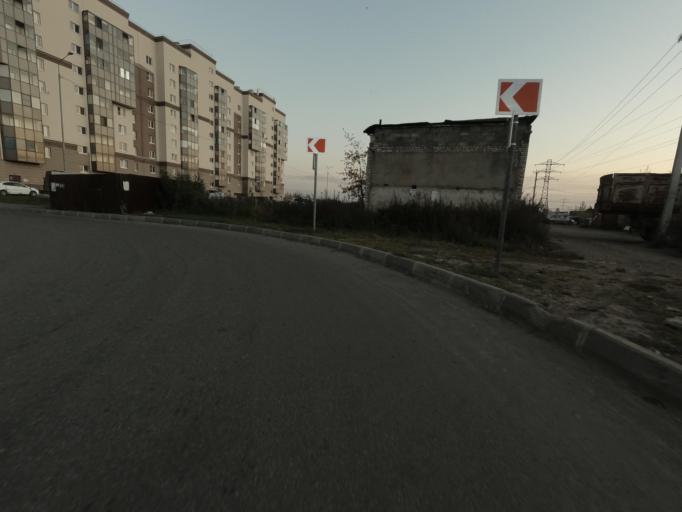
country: RU
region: Leningrad
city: Kirovsk
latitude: 59.8780
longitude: 31.0039
